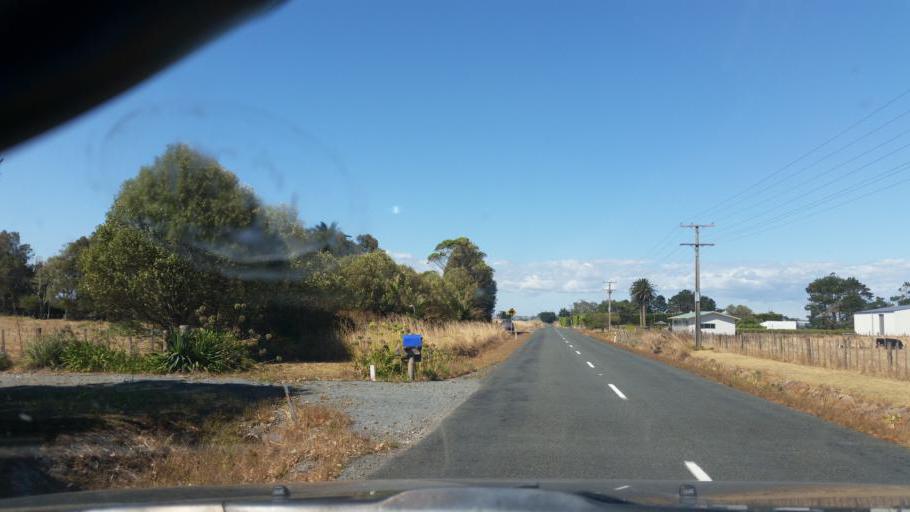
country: NZ
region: Northland
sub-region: Kaipara District
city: Dargaville
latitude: -35.9450
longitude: 173.8167
